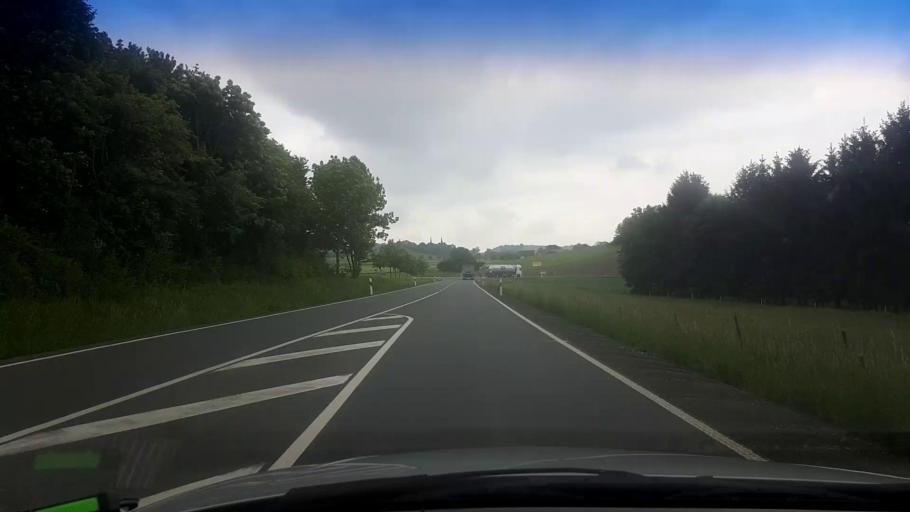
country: DE
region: Bavaria
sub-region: Upper Franconia
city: Goldkronach
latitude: 50.0058
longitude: 11.6790
